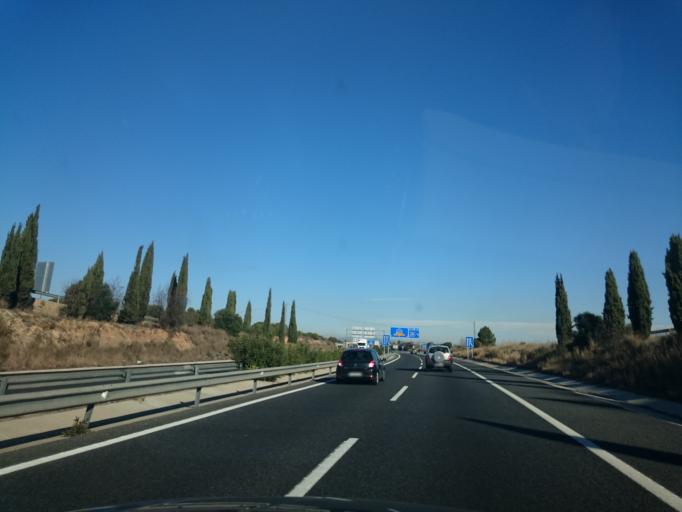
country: ES
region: Catalonia
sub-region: Provincia de Tarragona
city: Vila-seca
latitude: 41.1059
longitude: 1.1557
